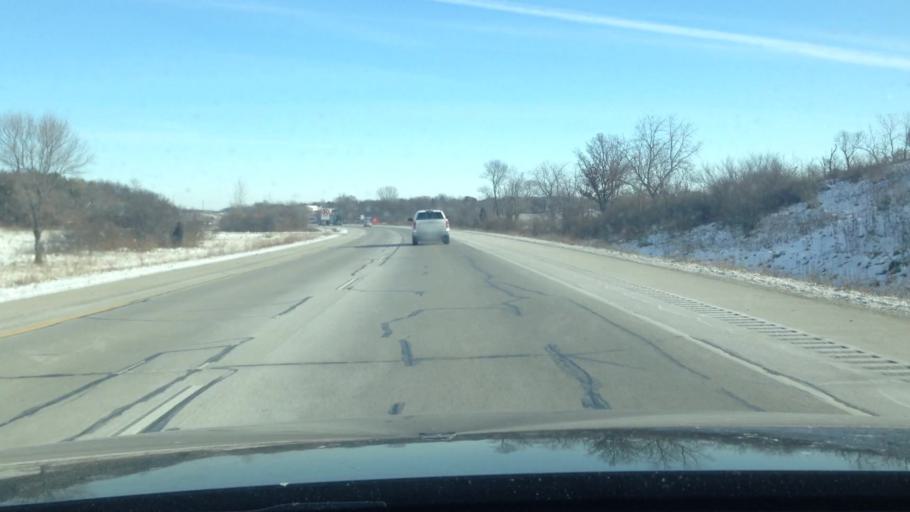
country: US
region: Wisconsin
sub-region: Waukesha County
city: Big Bend
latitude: 42.9129
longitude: -88.2107
